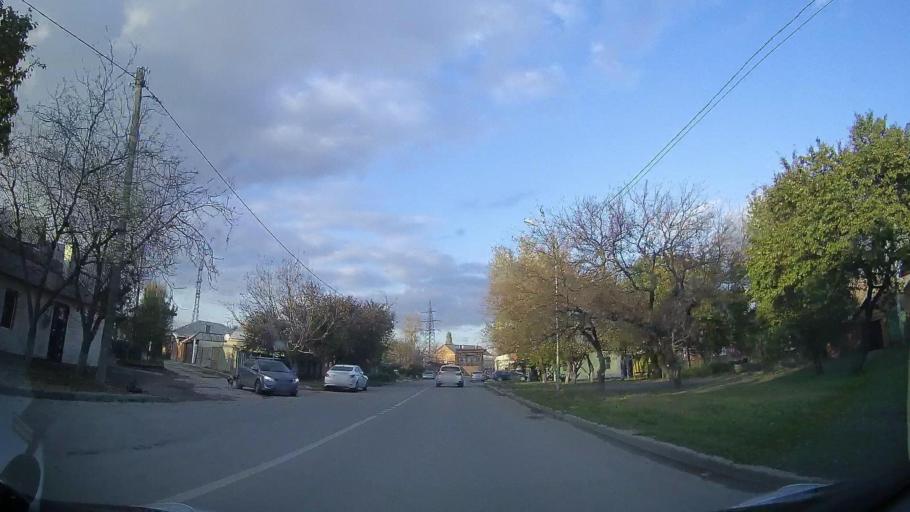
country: RU
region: Rostov
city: Imeni Chkalova
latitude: 47.2454
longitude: 39.7780
